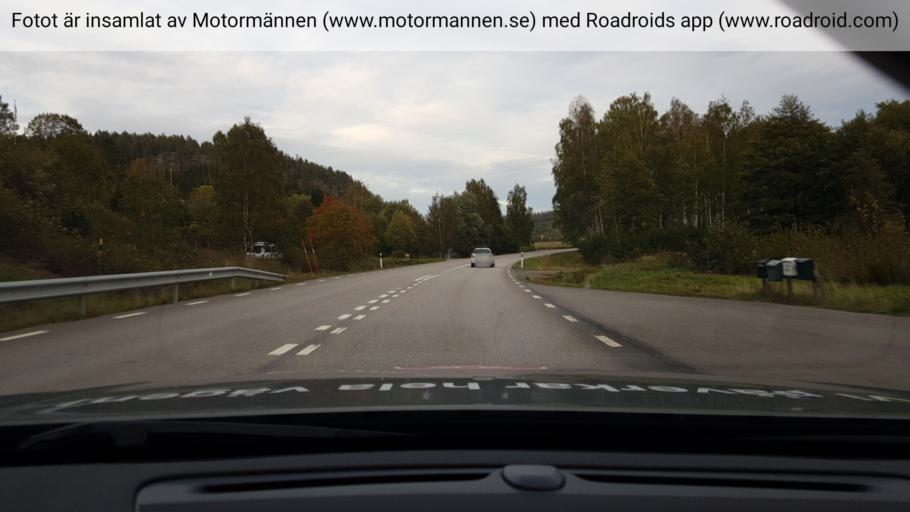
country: SE
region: Vaestra Goetaland
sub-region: Bengtsfors Kommun
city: Bengtsfors
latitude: 59.0371
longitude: 12.3186
